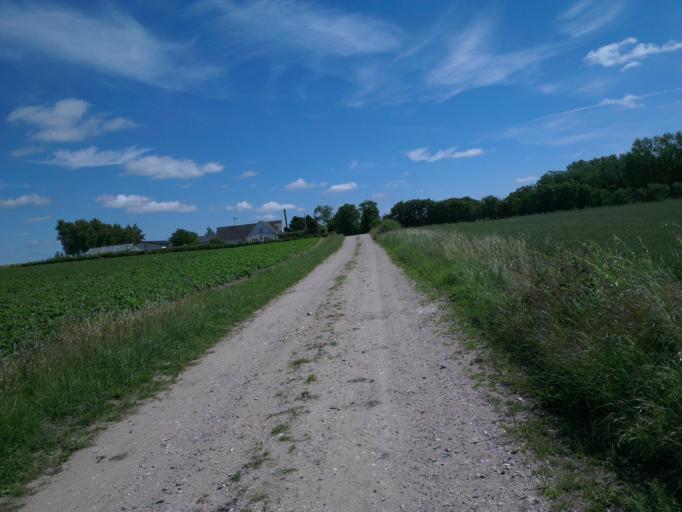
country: DK
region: Capital Region
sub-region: Frederikssund Kommune
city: Skibby
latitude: 55.7951
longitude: 11.9918
